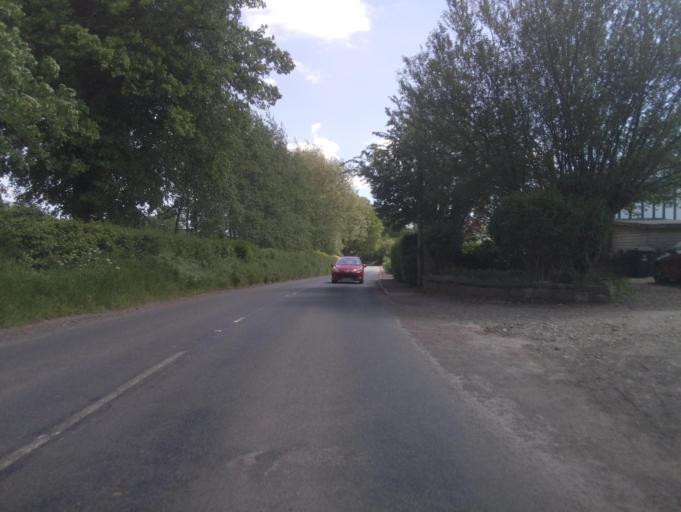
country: GB
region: Wales
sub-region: Monmouthshire
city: Monmouth
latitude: 51.8189
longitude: -2.7334
